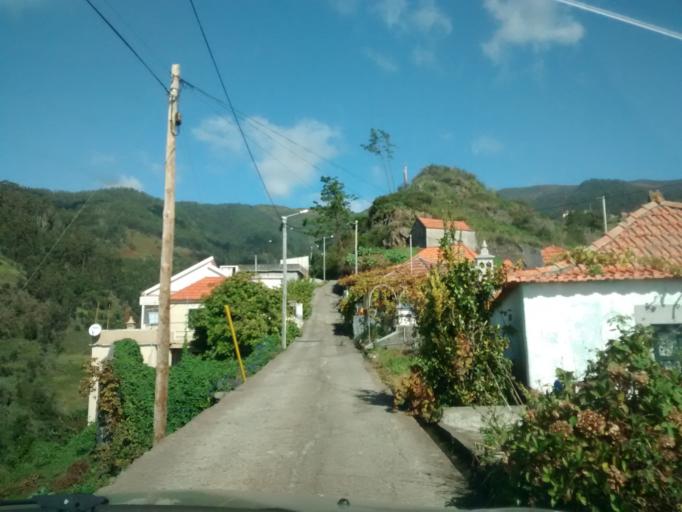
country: PT
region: Madeira
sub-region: Calheta
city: Arco da Calheta
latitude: 32.7318
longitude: -17.1593
